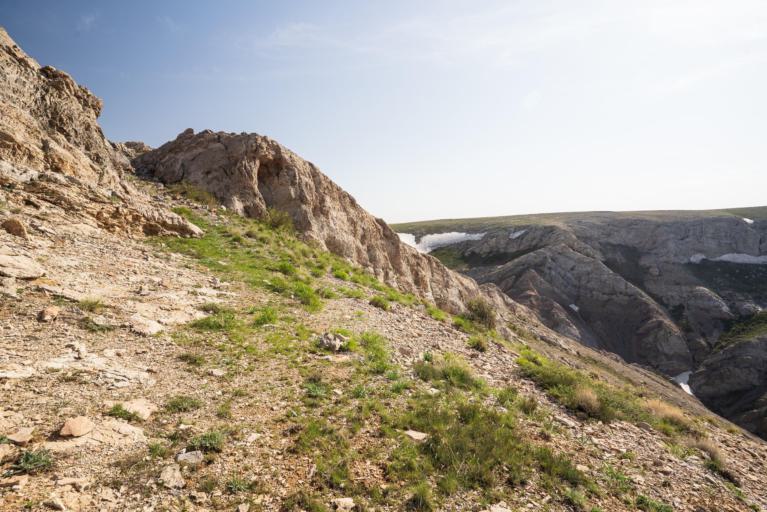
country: KZ
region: Ongtustik Qazaqstan
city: Kentau
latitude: 43.8605
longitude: 68.4166
